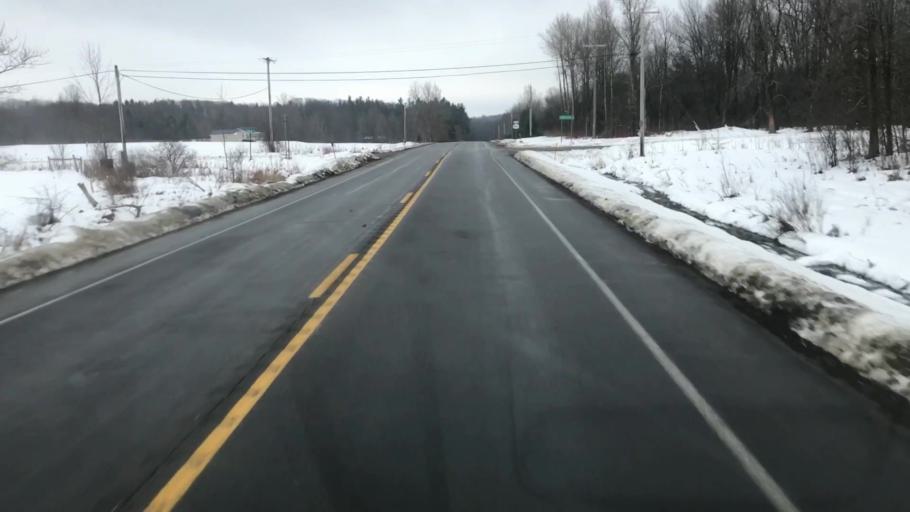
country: US
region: New York
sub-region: Cayuga County
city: Moravia
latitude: 42.7592
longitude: -76.3314
